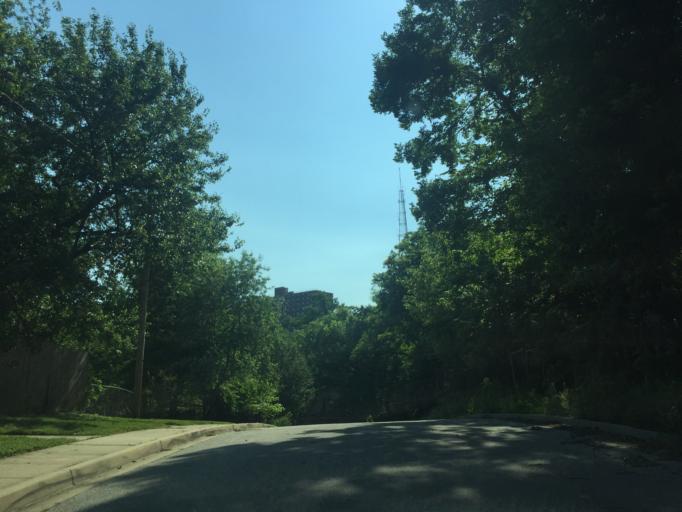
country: US
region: Maryland
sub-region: City of Baltimore
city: Baltimore
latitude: 39.3325
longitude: -76.6535
